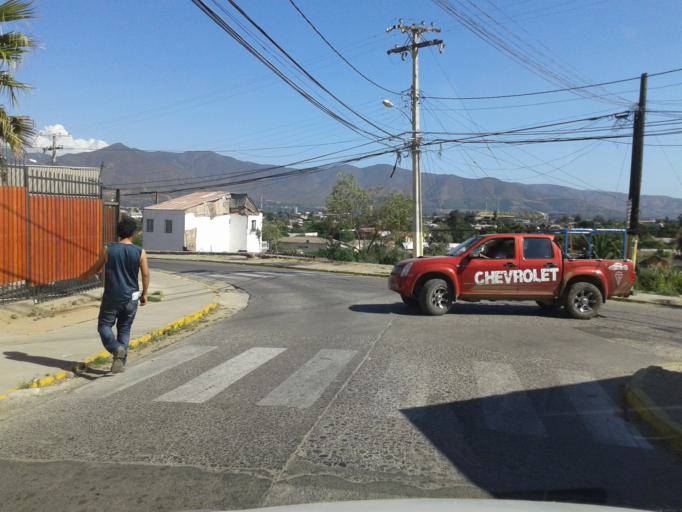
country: CL
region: Valparaiso
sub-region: Provincia de Quillota
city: Quillota
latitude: -32.8761
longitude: -71.2524
